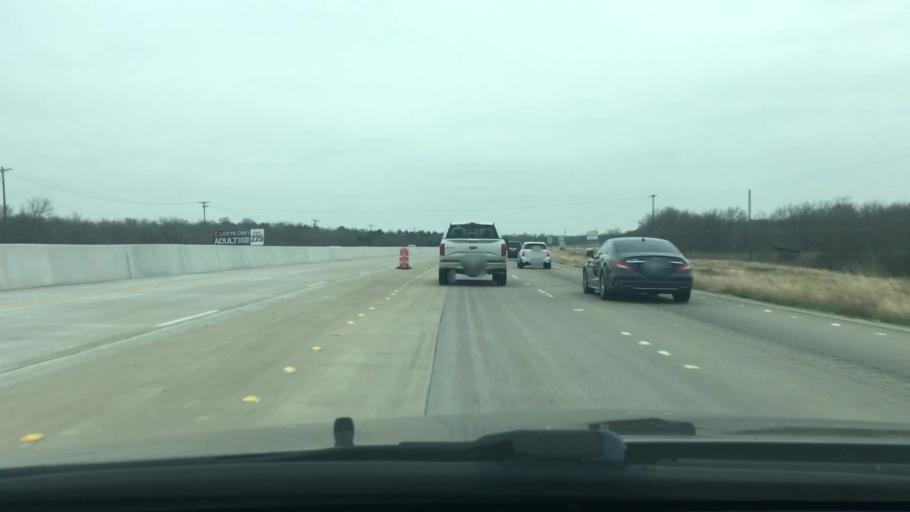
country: US
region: Texas
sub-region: Navarro County
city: Corsicana
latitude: 32.0886
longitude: -96.4392
